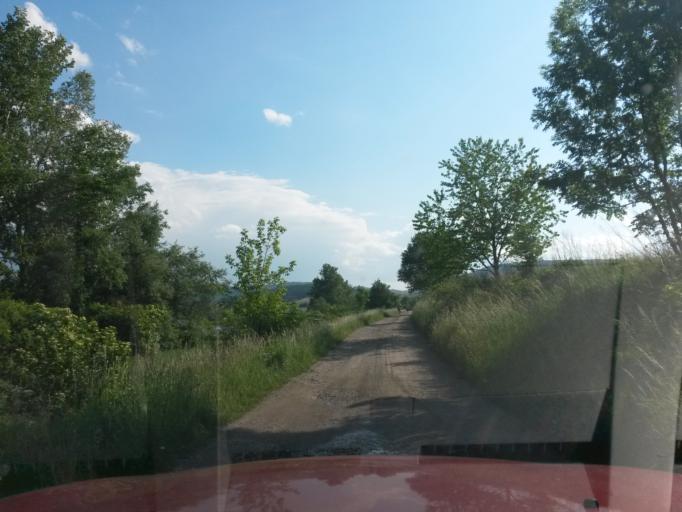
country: SK
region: Kosicky
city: Roznava
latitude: 48.5868
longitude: 20.6444
